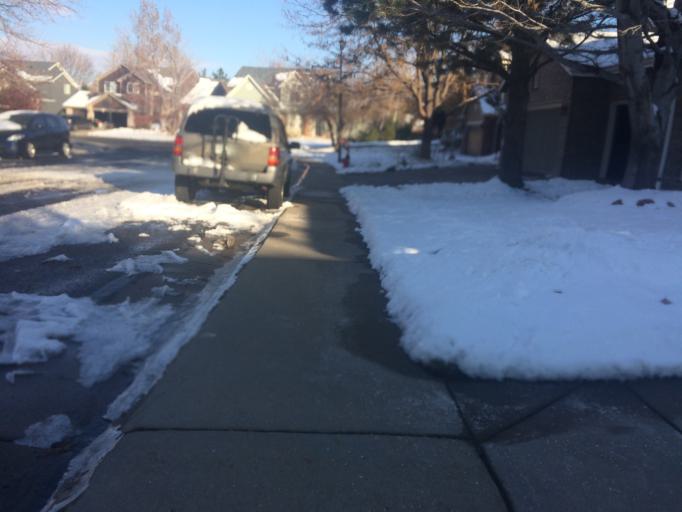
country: US
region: Colorado
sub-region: Boulder County
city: Louisville
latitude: 39.9927
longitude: -105.1197
